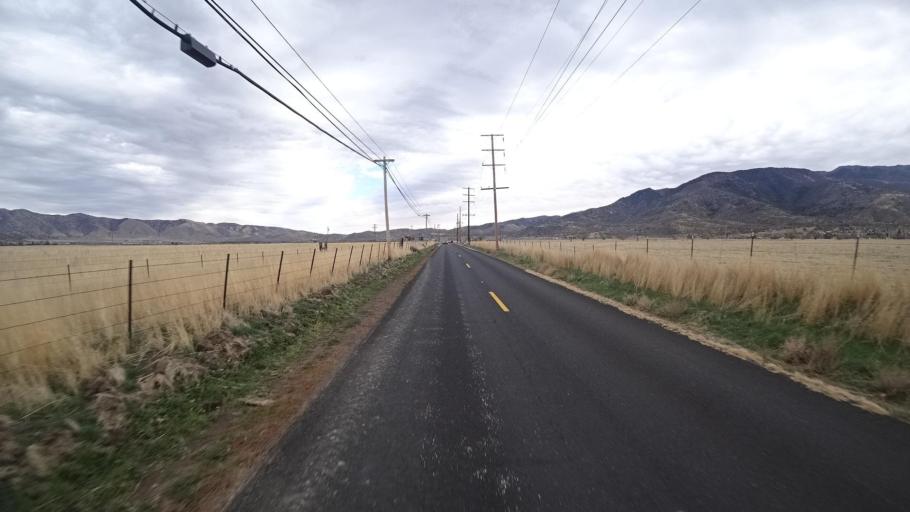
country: US
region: California
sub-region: Kern County
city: Stallion Springs
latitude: 35.0945
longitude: -118.6268
